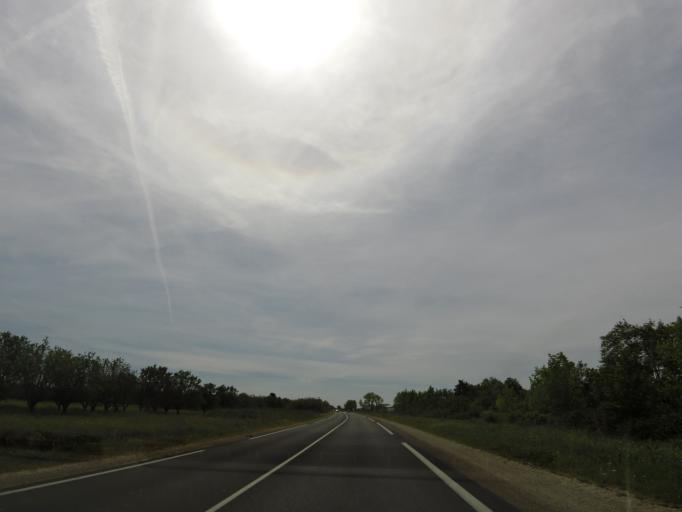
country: FR
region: Languedoc-Roussillon
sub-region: Departement de l'Herault
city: Lunel
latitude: 43.6588
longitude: 4.1380
